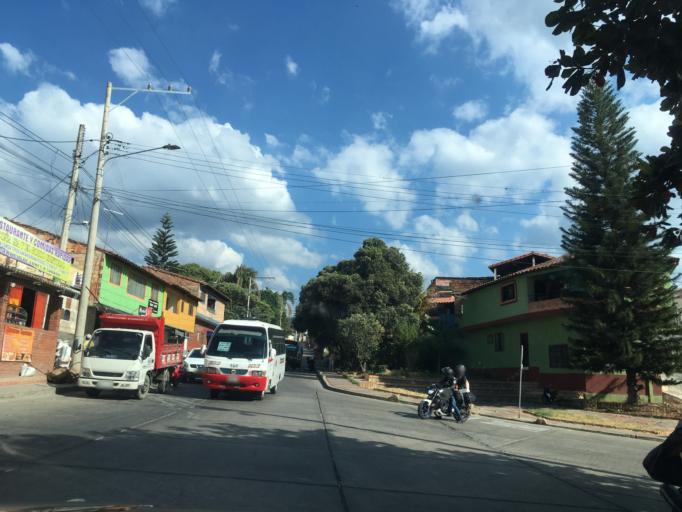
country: CO
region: Santander
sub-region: San Gil
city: San Gil
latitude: 6.5606
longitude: -73.1398
